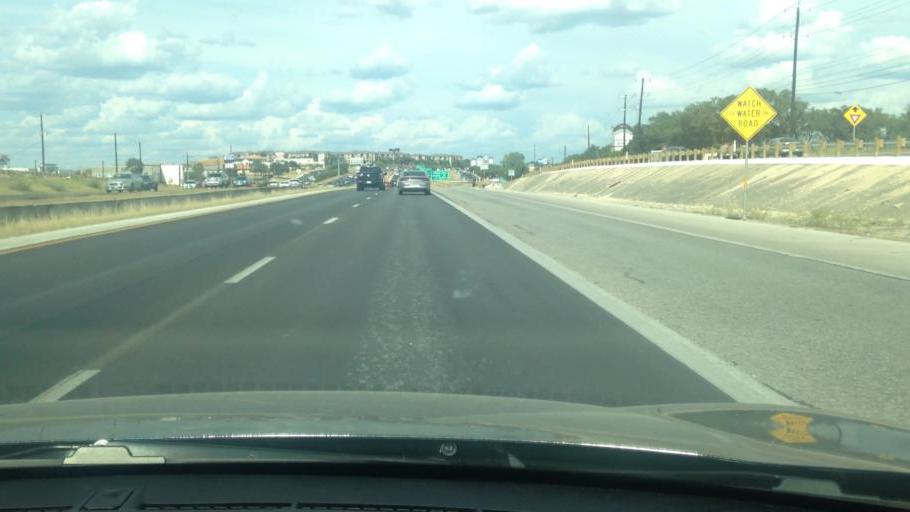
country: US
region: Texas
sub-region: Bexar County
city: Shavano Park
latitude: 29.5970
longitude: -98.5682
